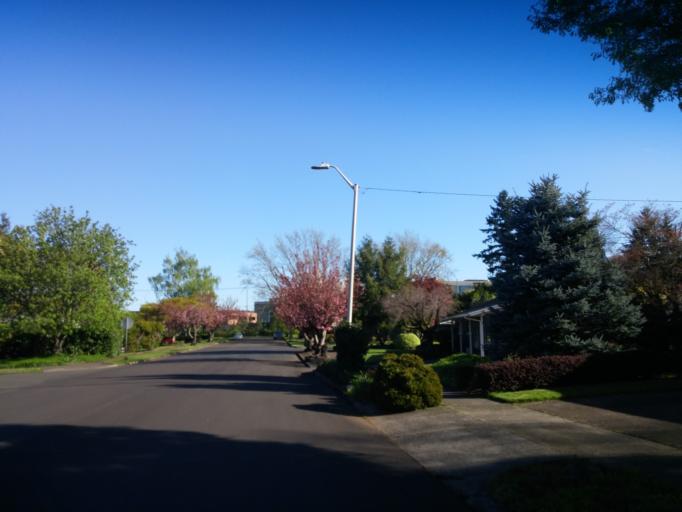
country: US
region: Oregon
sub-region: Washington County
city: West Slope
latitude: 45.5055
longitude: -122.7745
